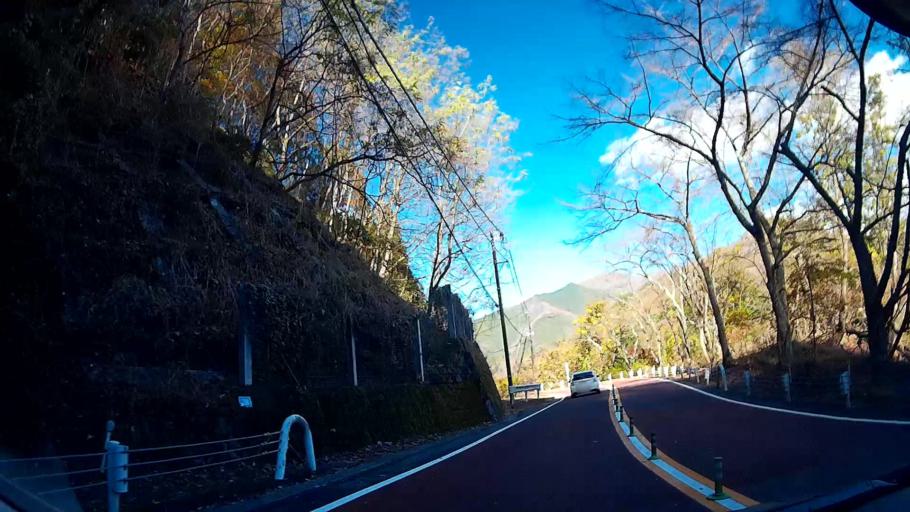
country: JP
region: Yamanashi
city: Uenohara
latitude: 35.7744
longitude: 139.0159
